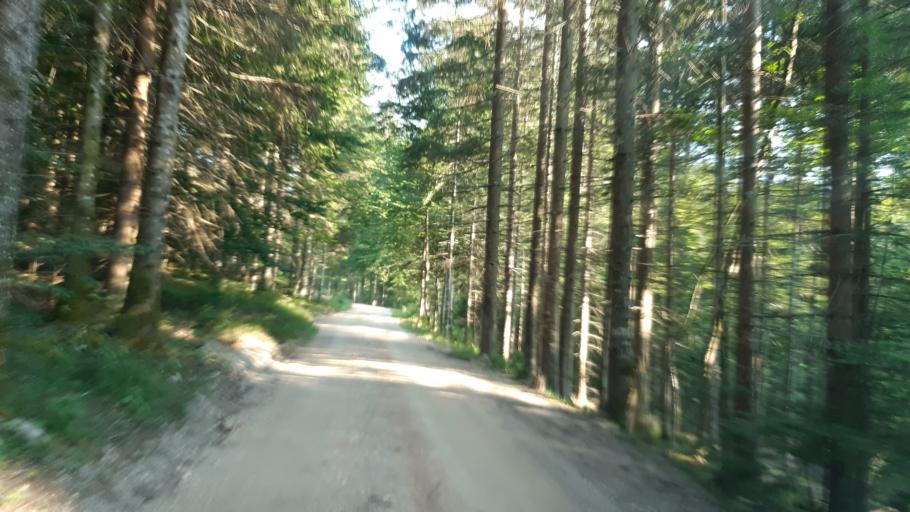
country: SI
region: Dolenjske Toplice
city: Dolenjske Toplice
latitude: 45.7021
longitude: 15.0102
